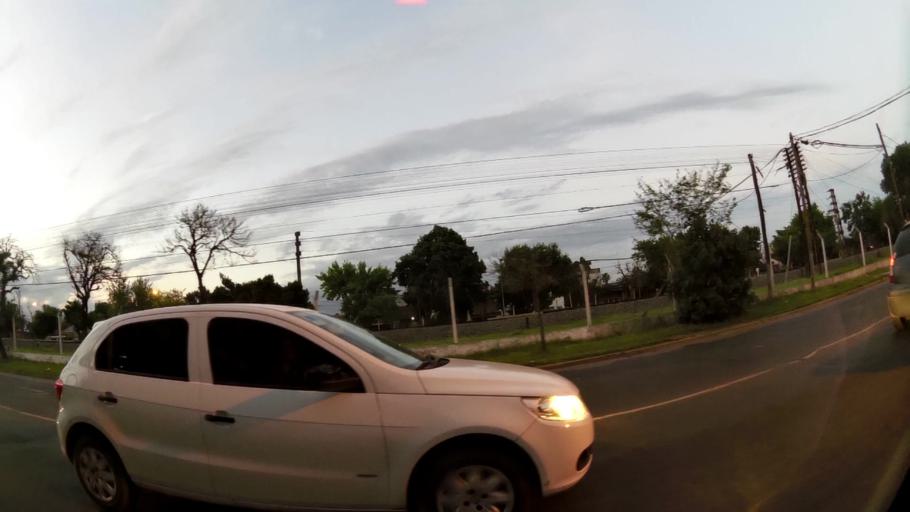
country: AR
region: Buenos Aires
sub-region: Partido de Merlo
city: Merlo
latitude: -34.6672
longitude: -58.7098
